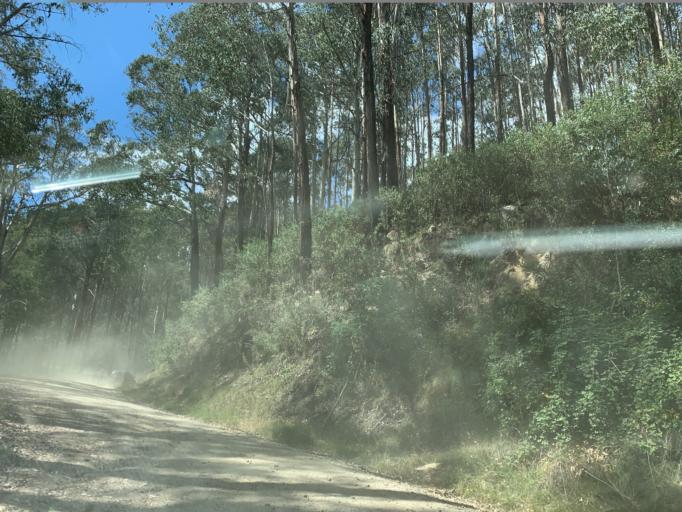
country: AU
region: Victoria
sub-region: Mansfield
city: Mansfield
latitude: -37.0935
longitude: 146.5389
